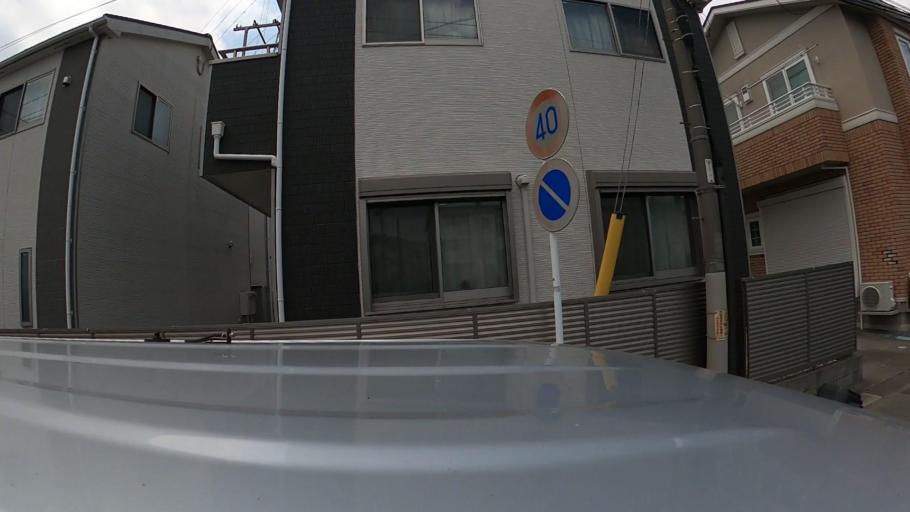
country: JP
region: Kanagawa
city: Chigasaki
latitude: 35.3743
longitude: 139.3952
